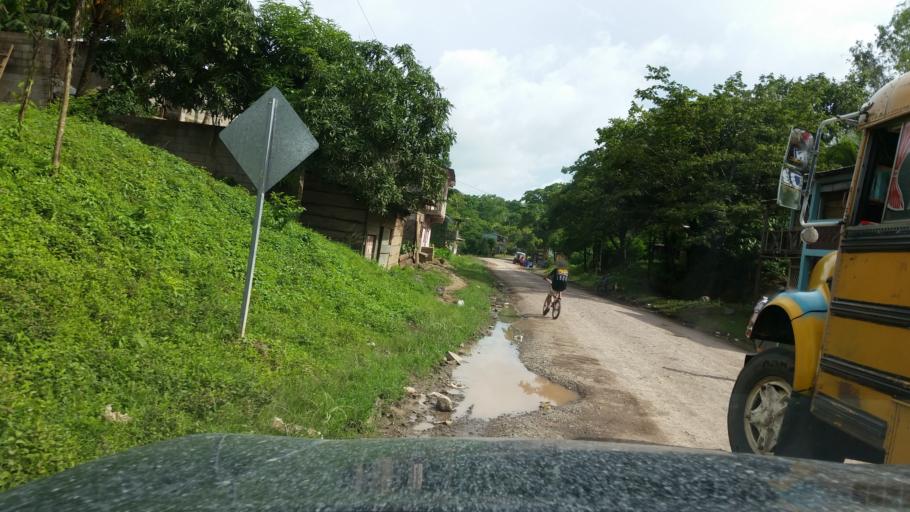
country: NI
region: Atlantico Norte (RAAN)
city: Siuna
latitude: 13.5909
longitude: -84.8120
